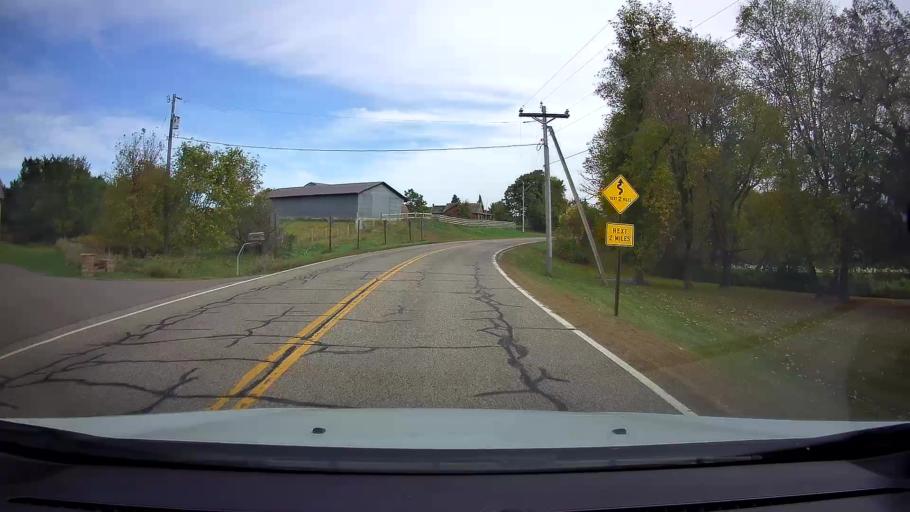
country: US
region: Minnesota
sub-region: Washington County
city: Stillwater
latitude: 45.1018
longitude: -92.8108
